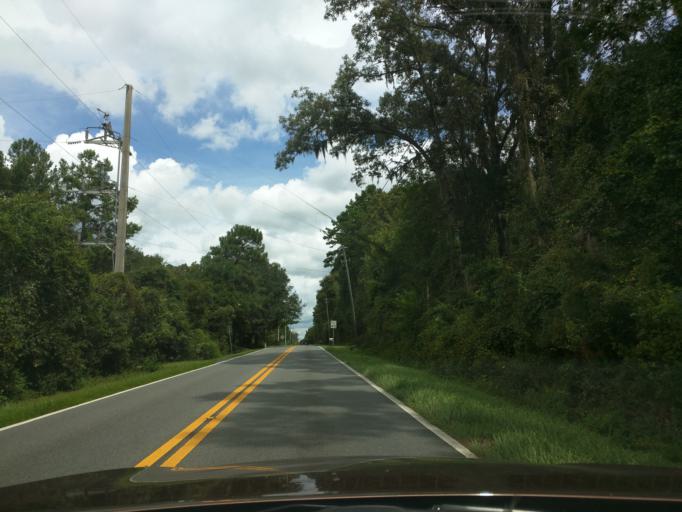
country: US
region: Florida
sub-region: Leon County
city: Tallahassee
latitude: 30.5401
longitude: -84.1764
